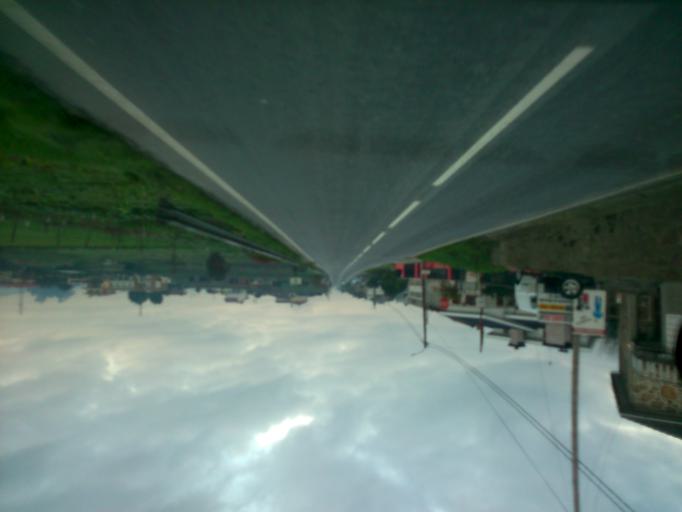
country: PT
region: Braga
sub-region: Barcelos
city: Barcelos
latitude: 41.5092
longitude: -8.5816
